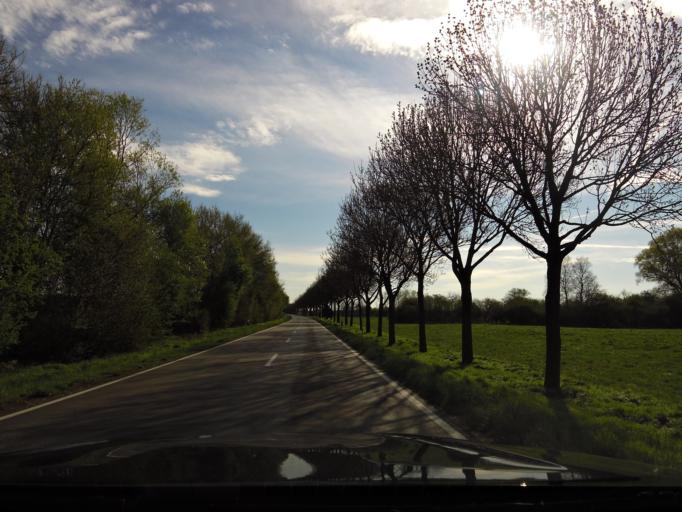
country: DE
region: Bavaria
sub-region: Upper Bavaria
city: Oberding
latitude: 48.3420
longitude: 11.8114
